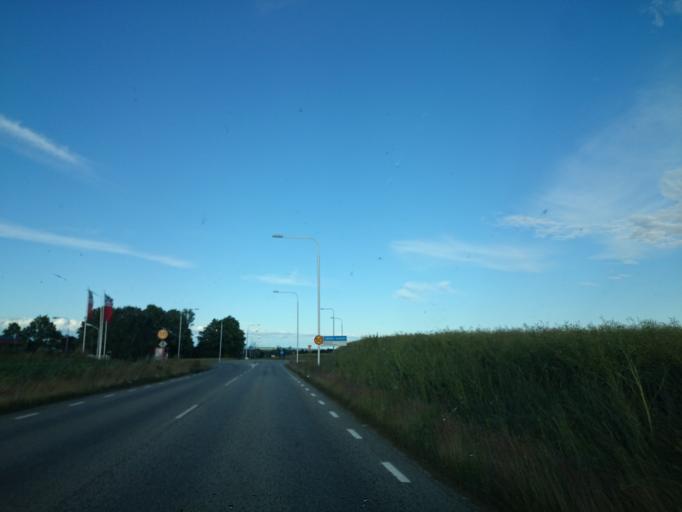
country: SE
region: Skane
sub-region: Eslovs Kommun
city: Eslov
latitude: 55.7177
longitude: 13.3298
